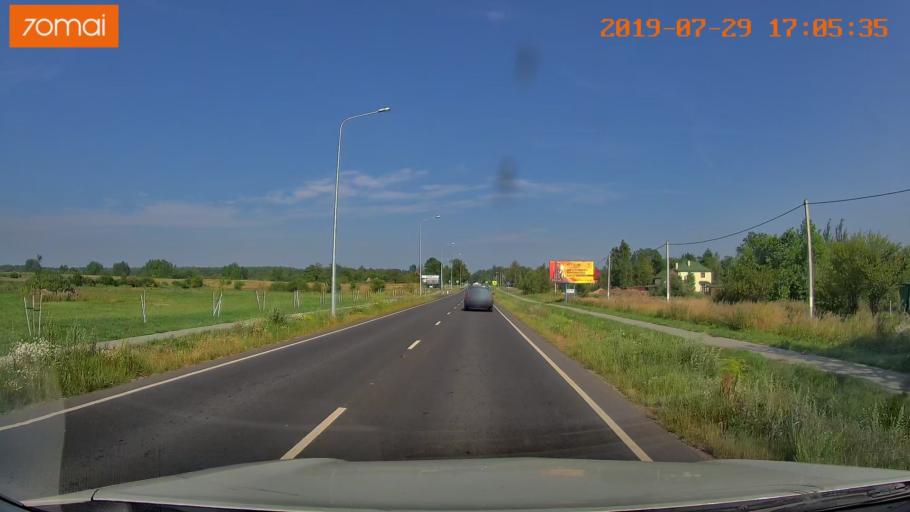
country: RU
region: Kaliningrad
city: Vzmorye
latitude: 54.8193
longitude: 20.2954
